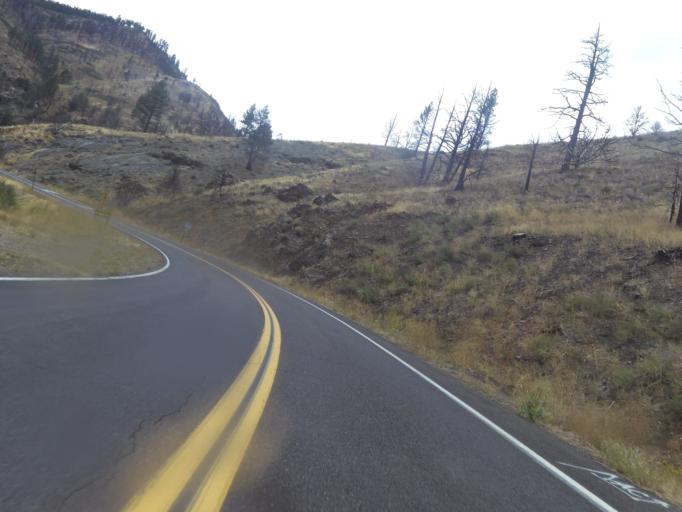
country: US
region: Nevada
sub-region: Douglas County
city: Gardnerville Ranchos
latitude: 38.6602
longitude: -119.7237
